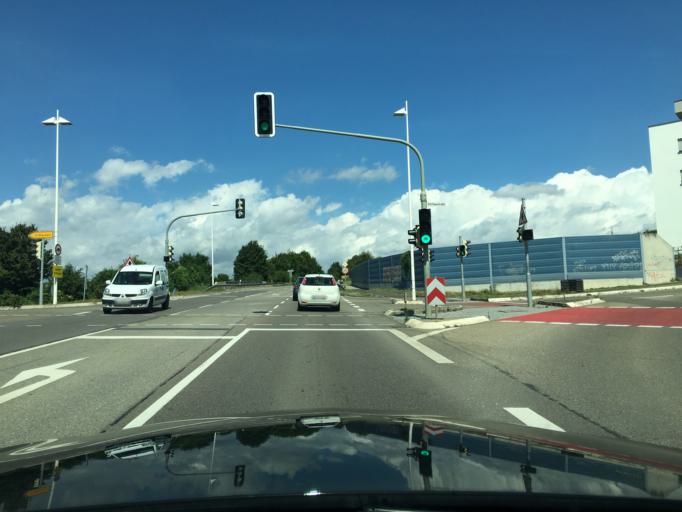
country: DE
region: Baden-Wuerttemberg
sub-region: Tuebingen Region
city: Dornstadt
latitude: 48.4143
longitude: 9.9373
